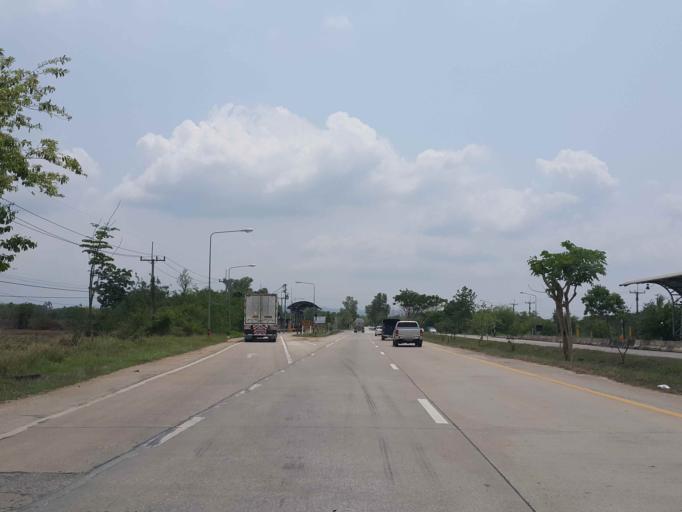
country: TH
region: Lampang
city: Ko Kha
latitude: 18.1867
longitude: 99.4077
